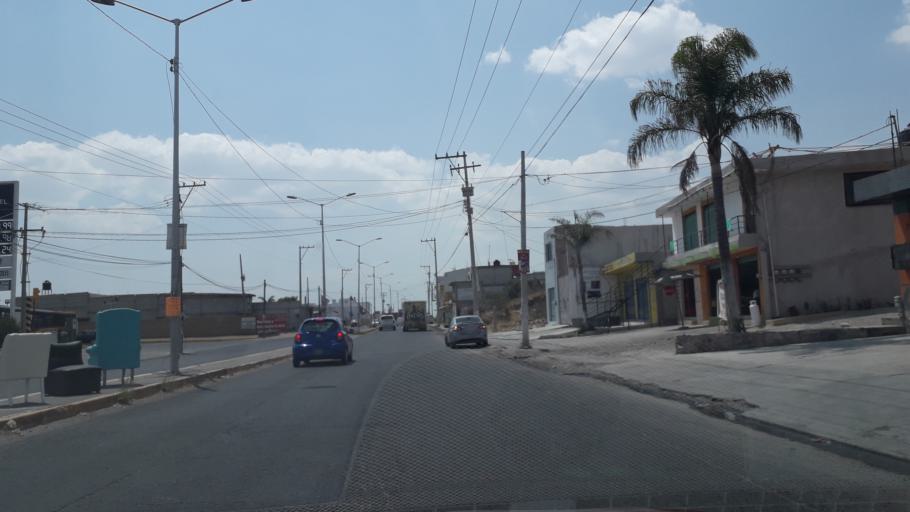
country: MX
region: Puebla
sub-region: Puebla
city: Galaxia la Calera
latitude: 18.9913
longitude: -98.1667
